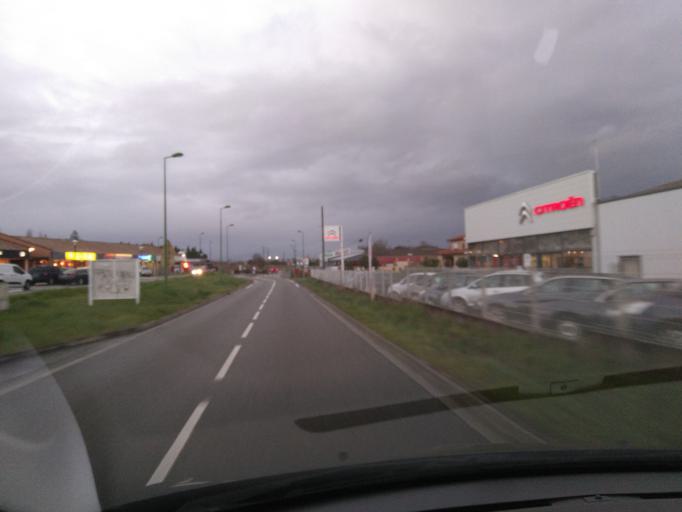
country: FR
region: Midi-Pyrenees
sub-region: Departement de la Haute-Garonne
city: Aussonne
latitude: 43.6875
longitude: 1.3360
